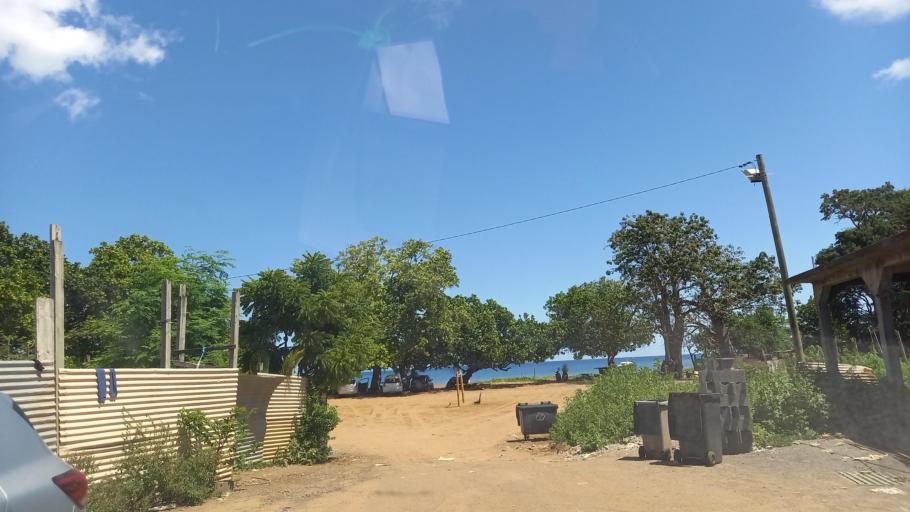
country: YT
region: Boueni
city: Boueni
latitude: -12.9238
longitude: 45.0890
